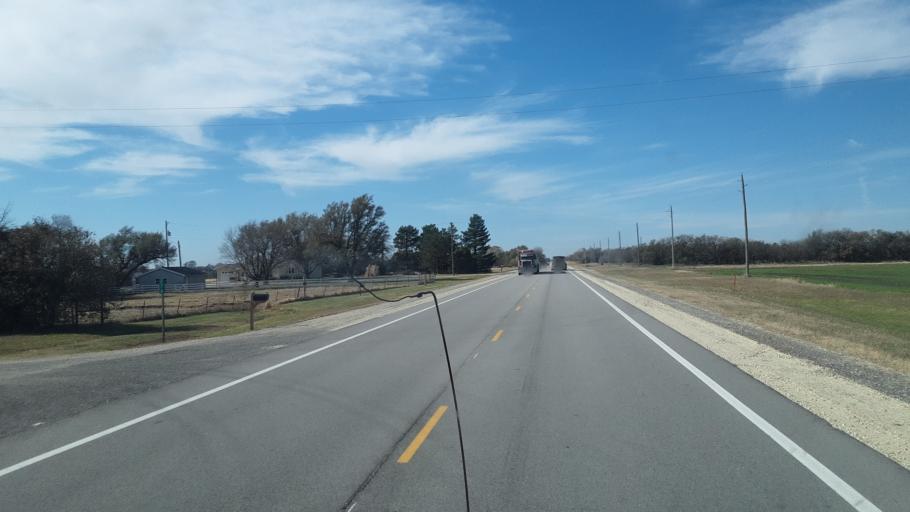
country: US
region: Kansas
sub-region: McPherson County
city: McPherson
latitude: 38.3768
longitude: -97.4882
